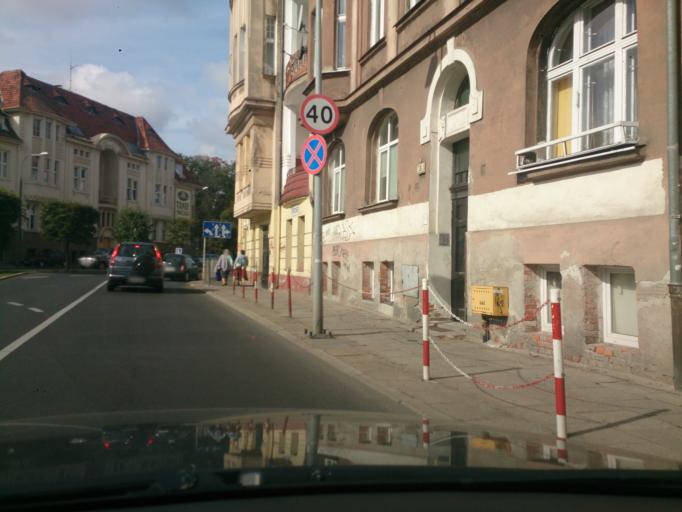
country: PL
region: Kujawsko-Pomorskie
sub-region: Bydgoszcz
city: Bydgoszcz
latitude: 53.1306
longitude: 18.0151
